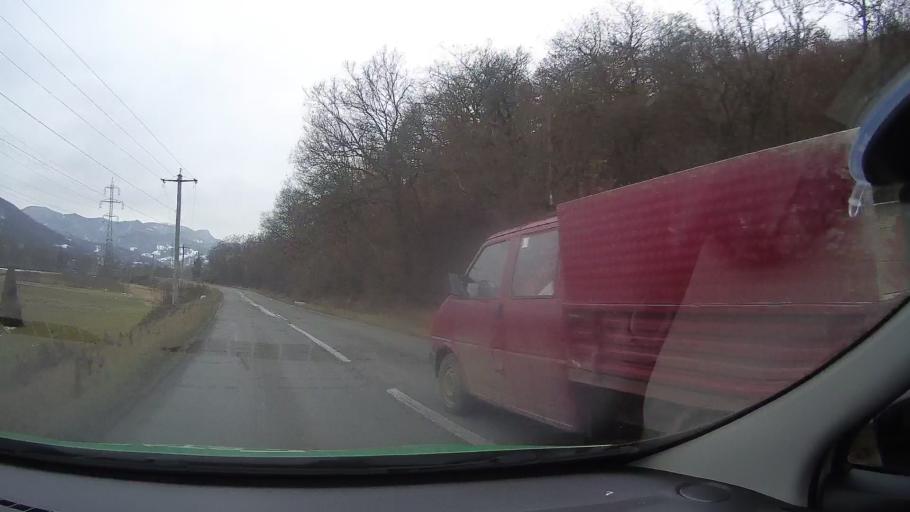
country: RO
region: Alba
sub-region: Comuna Ighiu
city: Ighiel
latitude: 46.1053
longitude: 23.4809
